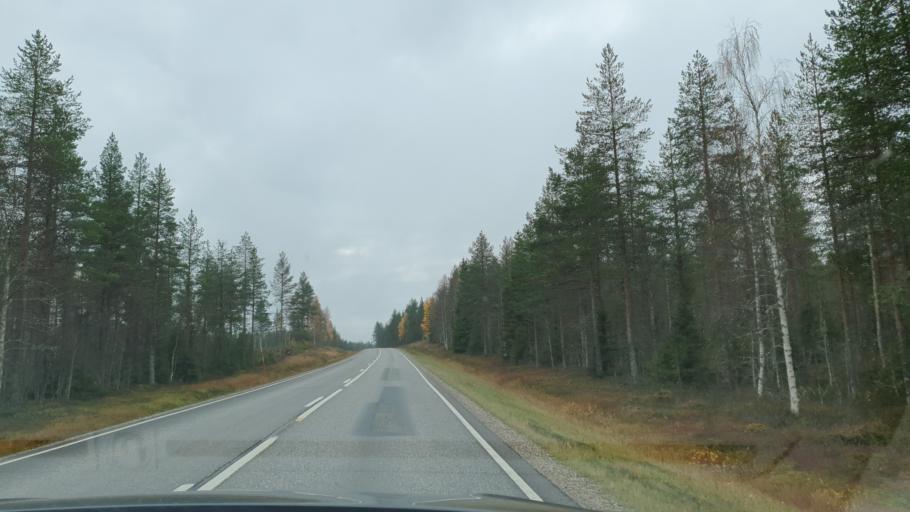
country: FI
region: Lapland
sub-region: Rovaniemi
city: Ranua
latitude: 66.0391
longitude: 26.3402
